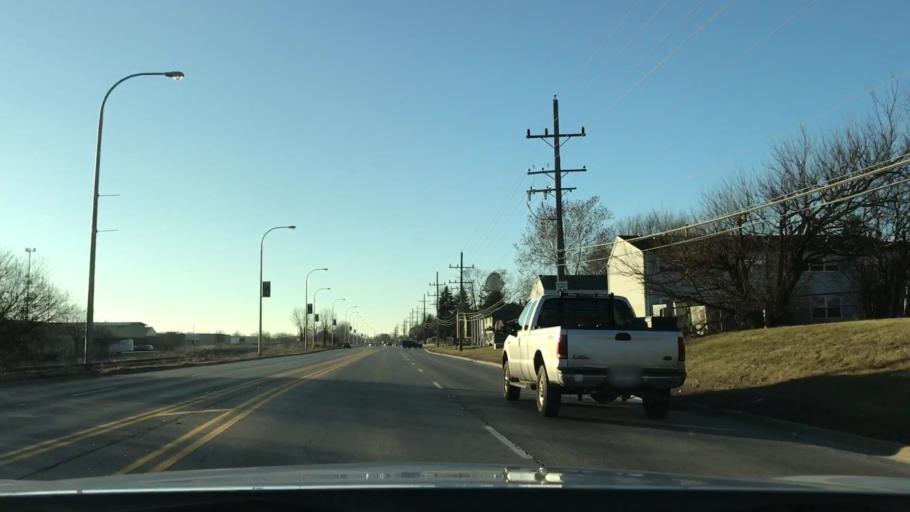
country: US
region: Illinois
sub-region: Kane County
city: Elgin
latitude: 42.0586
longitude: -88.3076
